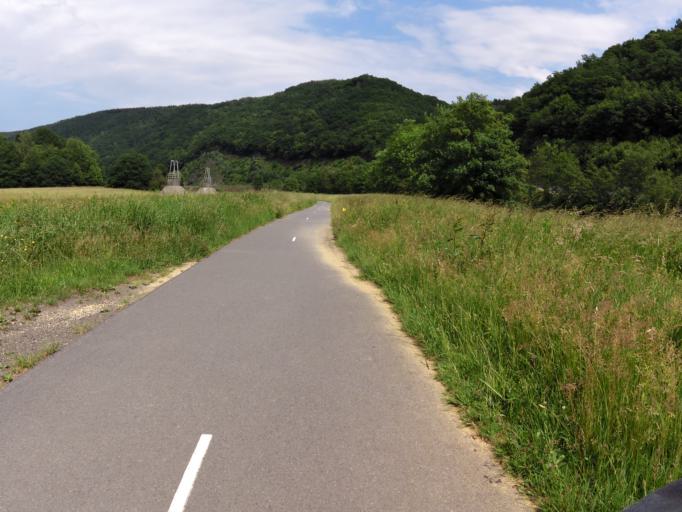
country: FR
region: Champagne-Ardenne
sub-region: Departement des Ardennes
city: Neufmanil
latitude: 49.8318
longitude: 4.7746
